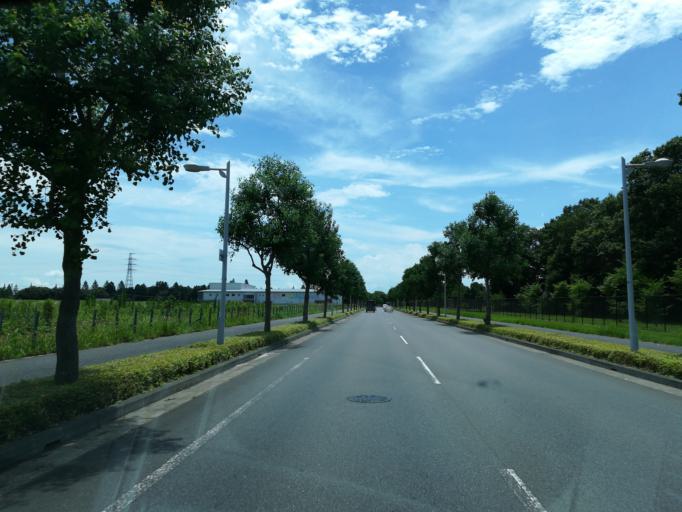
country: JP
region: Ibaraki
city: Naka
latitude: 36.0771
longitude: 140.0793
